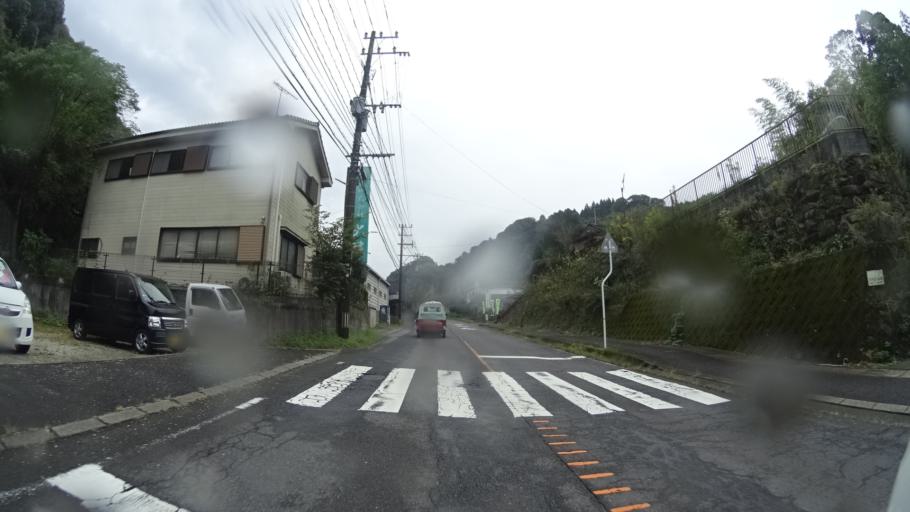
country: JP
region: Kagoshima
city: Kajiki
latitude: 31.7656
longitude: 130.6707
